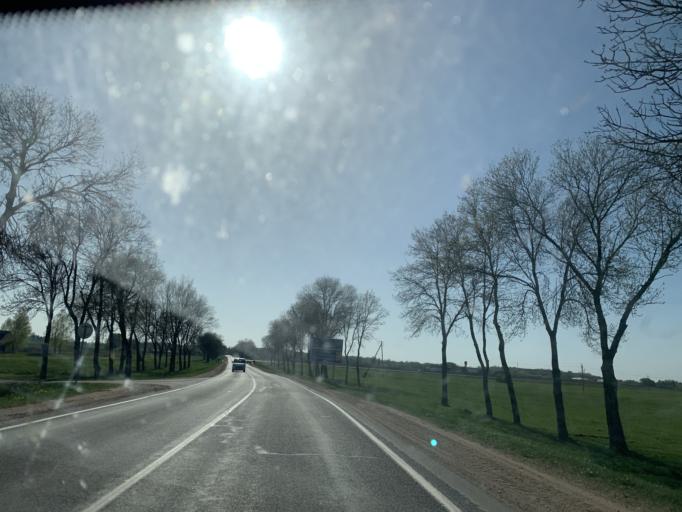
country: BY
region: Minsk
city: Nyasvizh
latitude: 53.2300
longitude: 26.7283
